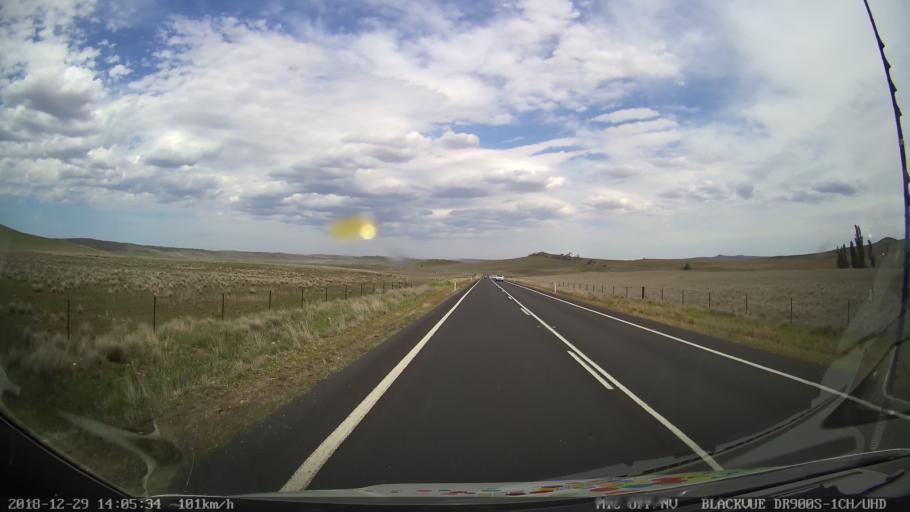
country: AU
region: New South Wales
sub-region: Cooma-Monaro
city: Cooma
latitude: -36.3323
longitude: 149.1928
